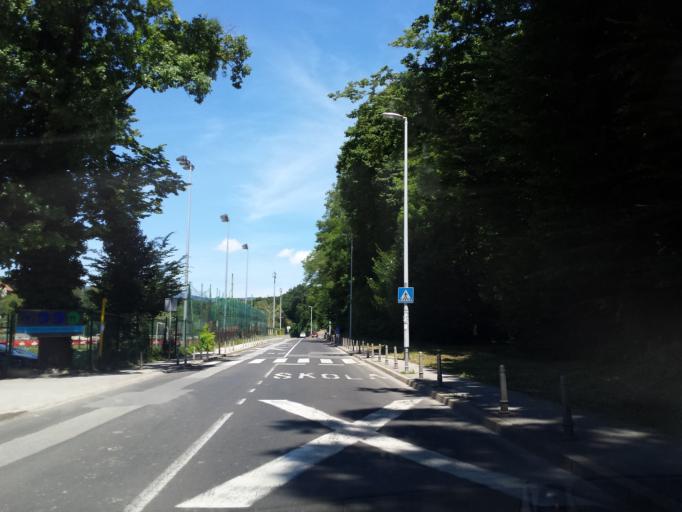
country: HR
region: Grad Zagreb
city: Zagreb
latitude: 45.8255
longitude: 16.0139
